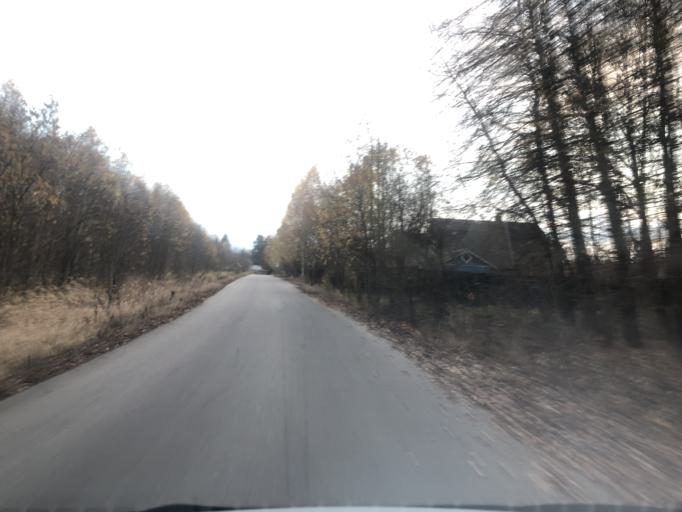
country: RU
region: Moskovskaya
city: Fryanovo
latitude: 56.1541
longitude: 38.3898
